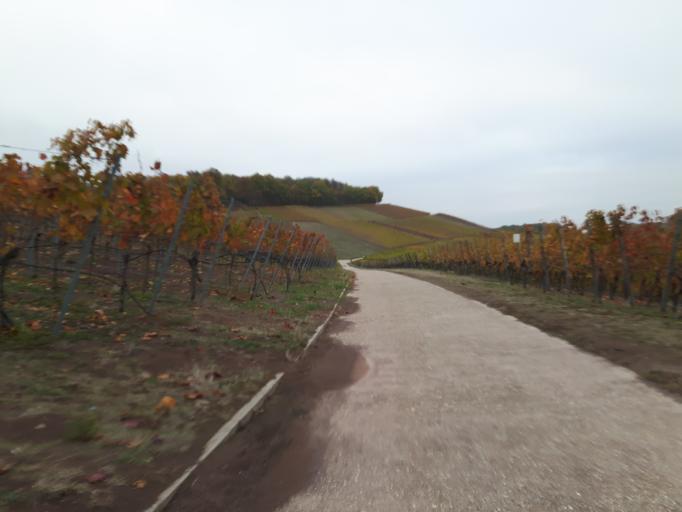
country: DE
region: Baden-Wuerttemberg
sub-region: Karlsruhe Region
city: Zaisenhausen
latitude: 49.1662
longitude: 8.8137
